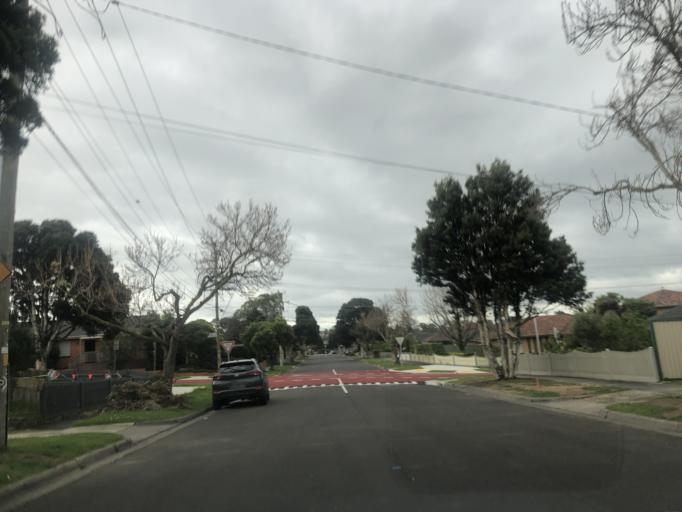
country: AU
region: Victoria
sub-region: Greater Dandenong
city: Dandenong North
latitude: -37.9629
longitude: 145.2220
